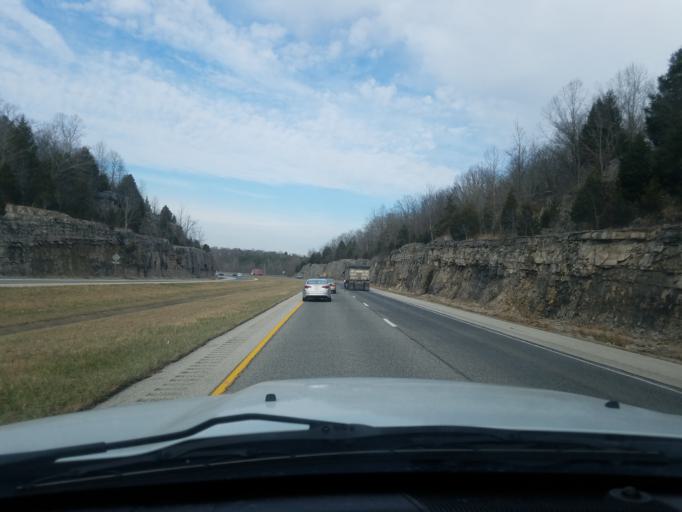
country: US
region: Indiana
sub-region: Lawrence County
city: Oolitic
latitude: 38.8759
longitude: -86.5189
